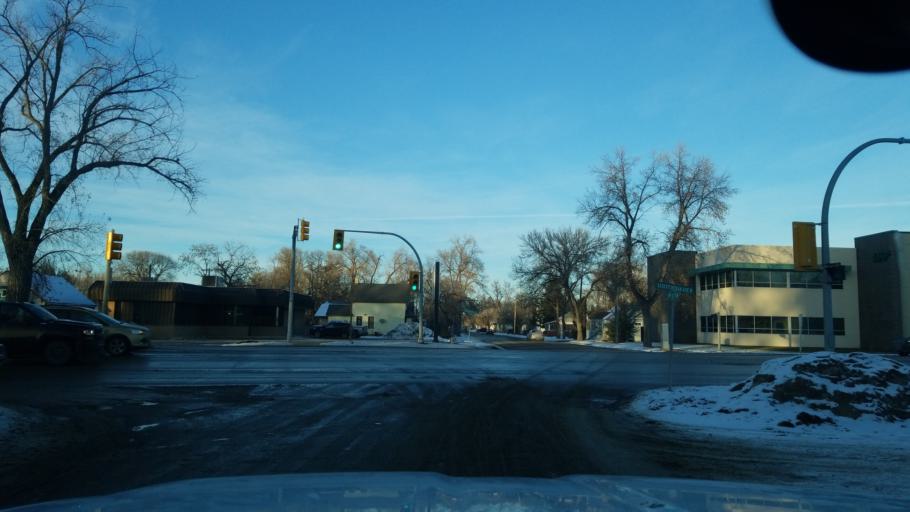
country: CA
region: Manitoba
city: Portage la Prairie
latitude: 49.9733
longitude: -98.3017
